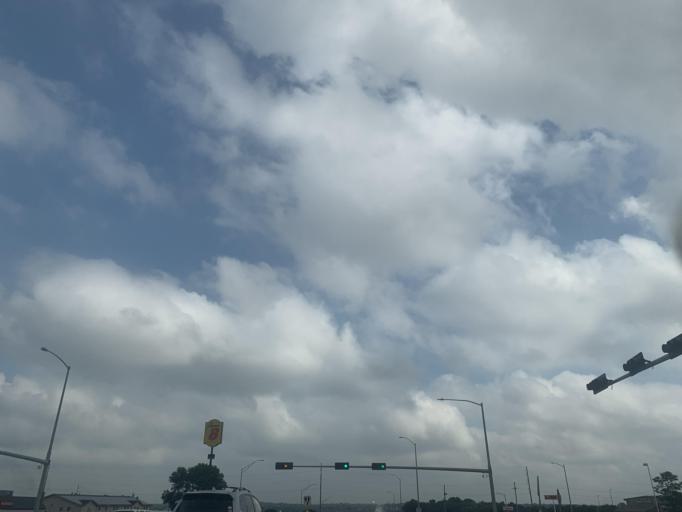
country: US
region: Nebraska
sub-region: Sarpy County
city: Chalco
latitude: 41.1652
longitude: -96.1388
